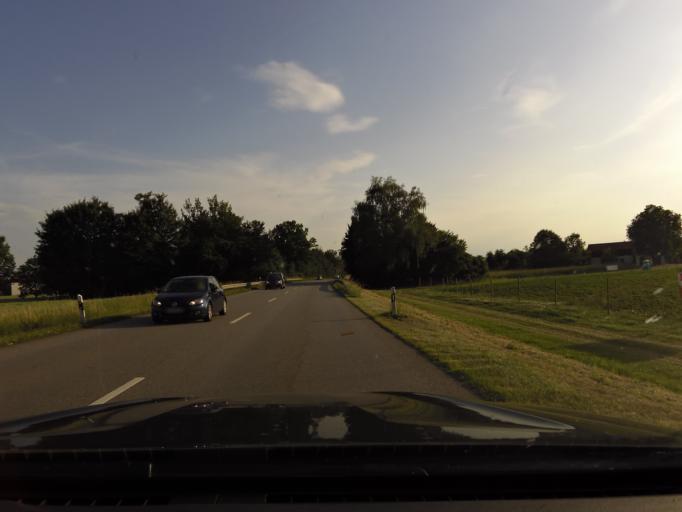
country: DE
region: Bavaria
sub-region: Upper Bavaria
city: Altoetting
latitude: 48.2311
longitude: 12.6628
